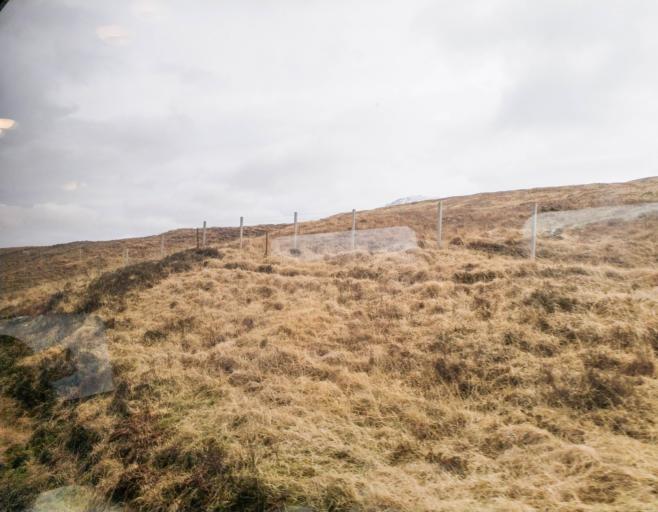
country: GB
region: Scotland
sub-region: Highland
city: Spean Bridge
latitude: 56.5417
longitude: -4.7584
